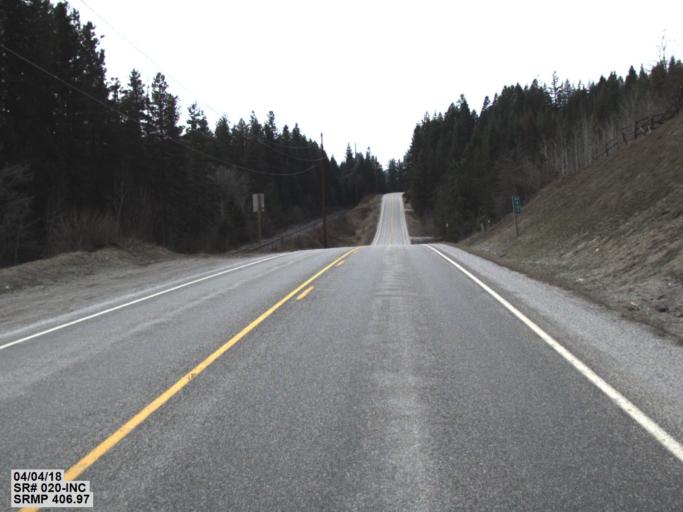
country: US
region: Washington
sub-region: Pend Oreille County
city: Newport
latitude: 48.4840
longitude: -117.2716
